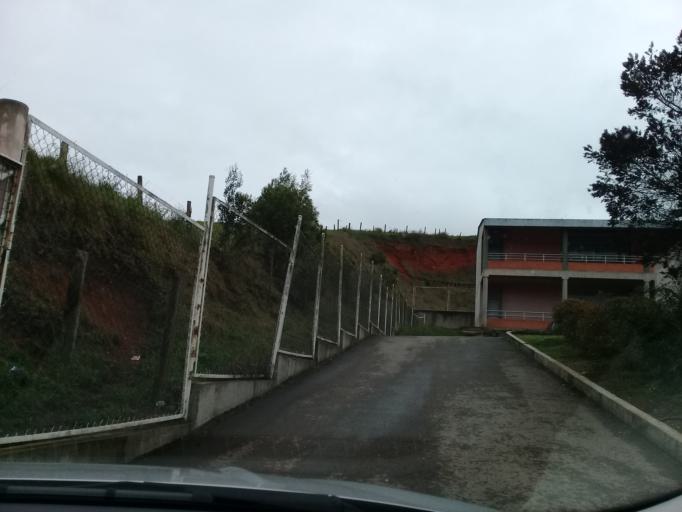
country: CO
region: Boyaca
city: Samaca
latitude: 5.4323
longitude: -73.4505
